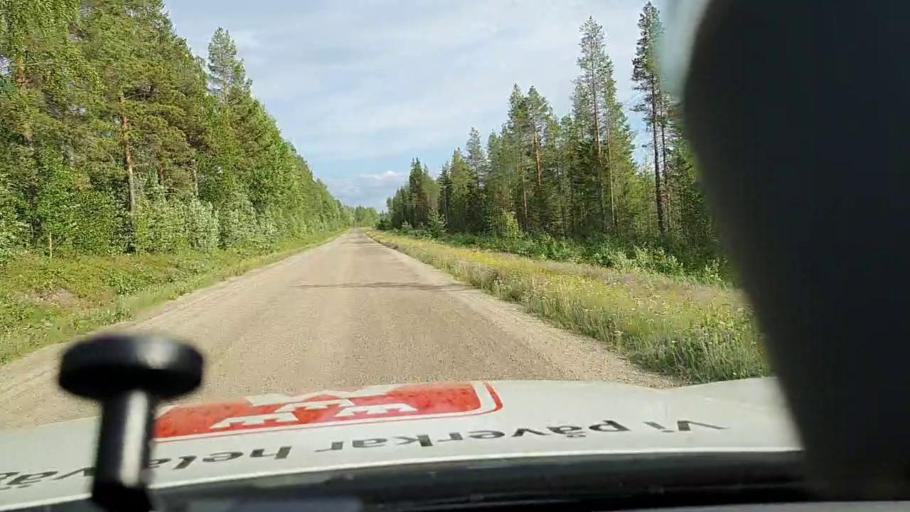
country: SE
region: Norrbotten
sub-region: Alvsbyns Kommun
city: AElvsbyn
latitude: 66.1797
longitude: 21.2305
